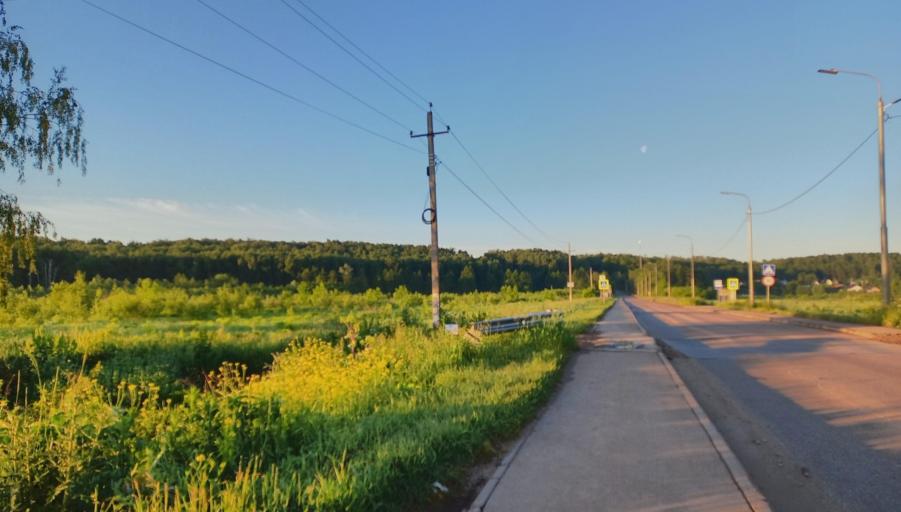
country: RU
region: Moskovskaya
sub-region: Leninskiy Rayon
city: Molokovo
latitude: 55.5723
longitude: 37.8396
